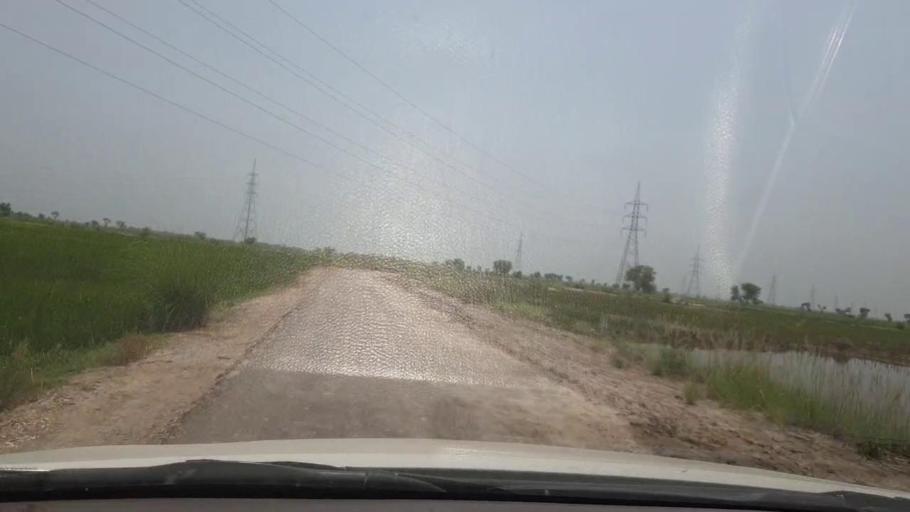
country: PK
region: Sindh
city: Shikarpur
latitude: 28.0935
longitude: 68.6172
